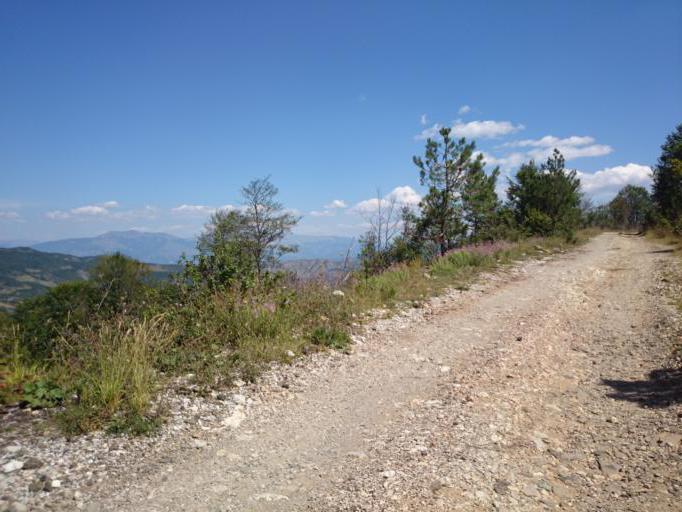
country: AL
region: Diber
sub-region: Rrethi i Bulqizes
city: Zerqan
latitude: 41.4332
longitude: 20.3262
